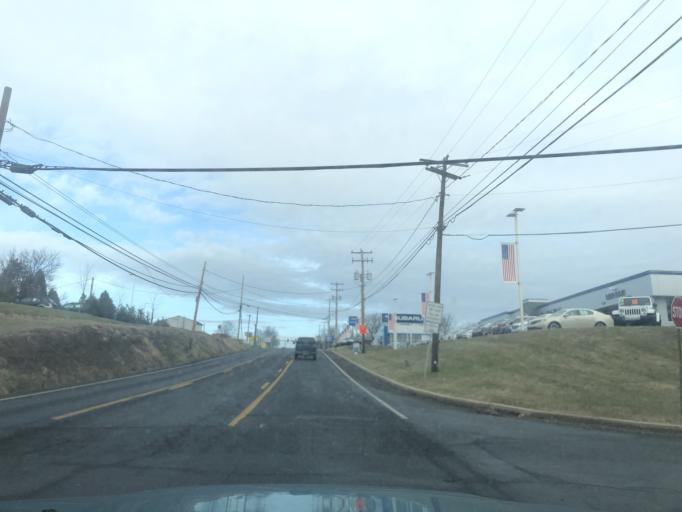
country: US
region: Pennsylvania
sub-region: Bucks County
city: Sellersville
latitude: 40.3429
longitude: -75.3035
